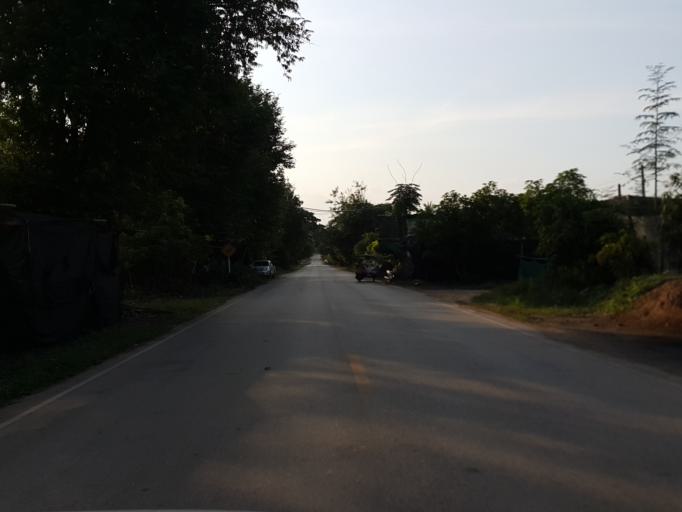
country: TH
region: Sukhothai
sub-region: Amphoe Si Satchanalai
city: Si Satchanalai
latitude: 17.4178
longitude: 99.7970
